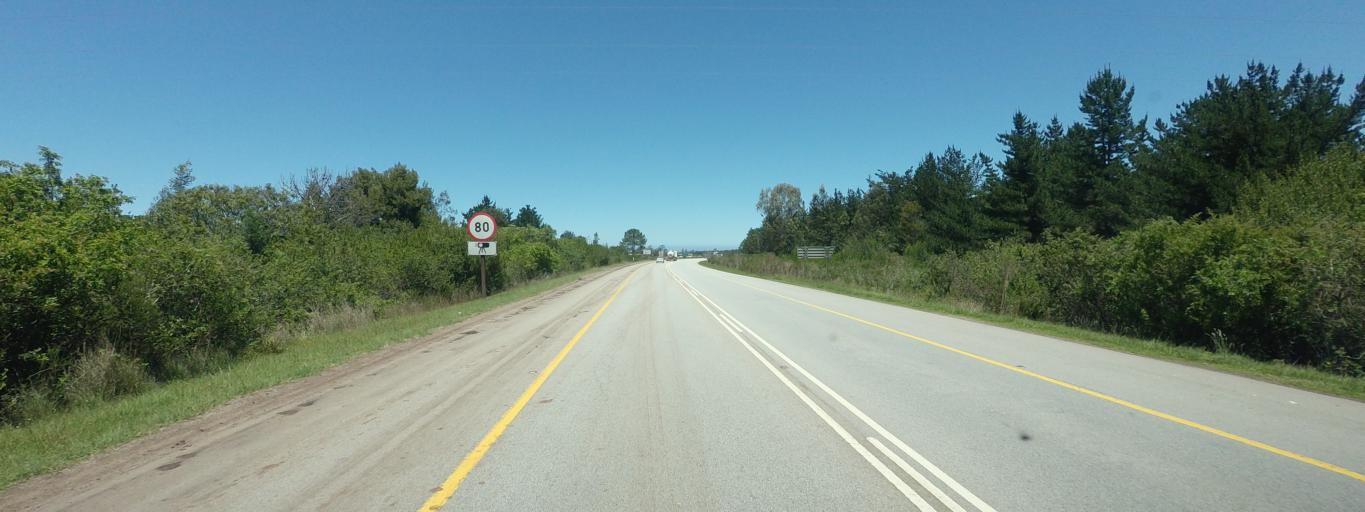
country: ZA
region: Western Cape
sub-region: Eden District Municipality
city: Plettenberg Bay
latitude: -33.9418
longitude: 23.4885
